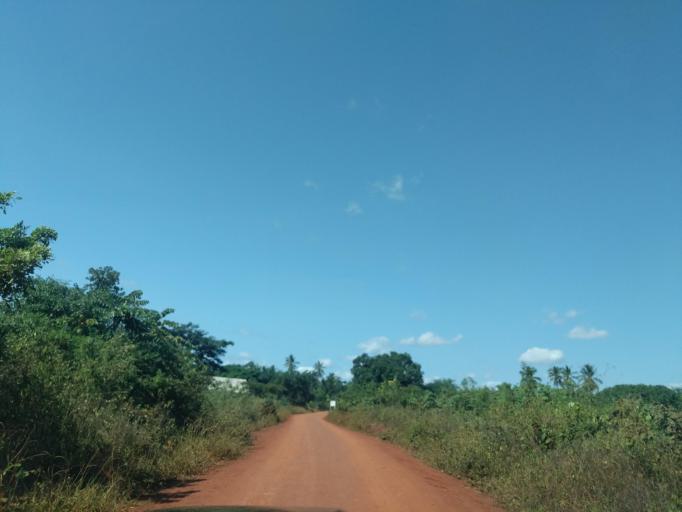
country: TZ
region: Tanga
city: Muheza
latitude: -5.3805
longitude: 38.5813
